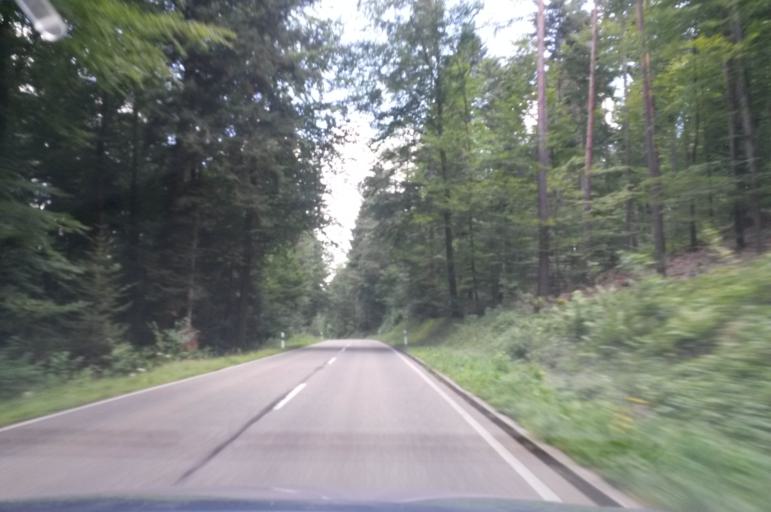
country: DE
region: Baden-Wuerttemberg
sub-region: Karlsruhe Region
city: Bad Herrenalb
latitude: 48.8688
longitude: 8.4529
